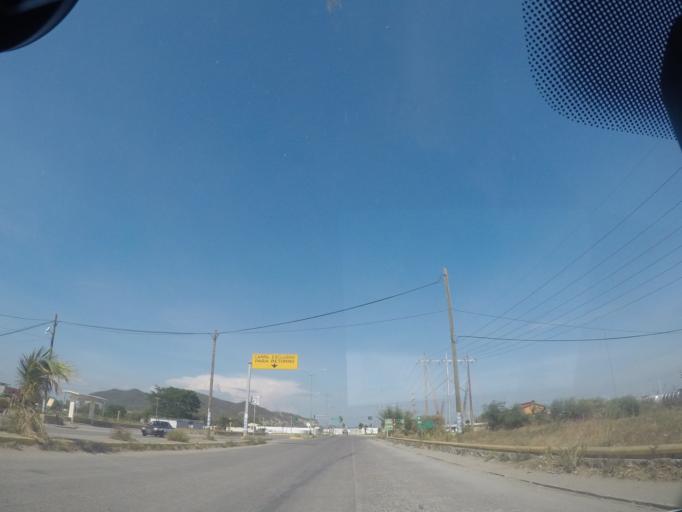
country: MX
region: Oaxaca
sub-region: Salina Cruz
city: Salina Cruz
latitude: 16.2198
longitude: -95.1915
